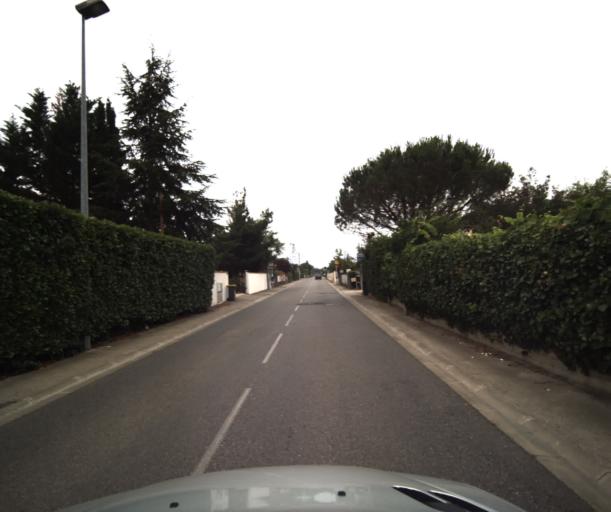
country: FR
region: Midi-Pyrenees
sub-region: Departement de la Haute-Garonne
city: Portet-sur-Garonne
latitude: 43.5194
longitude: 1.3965
